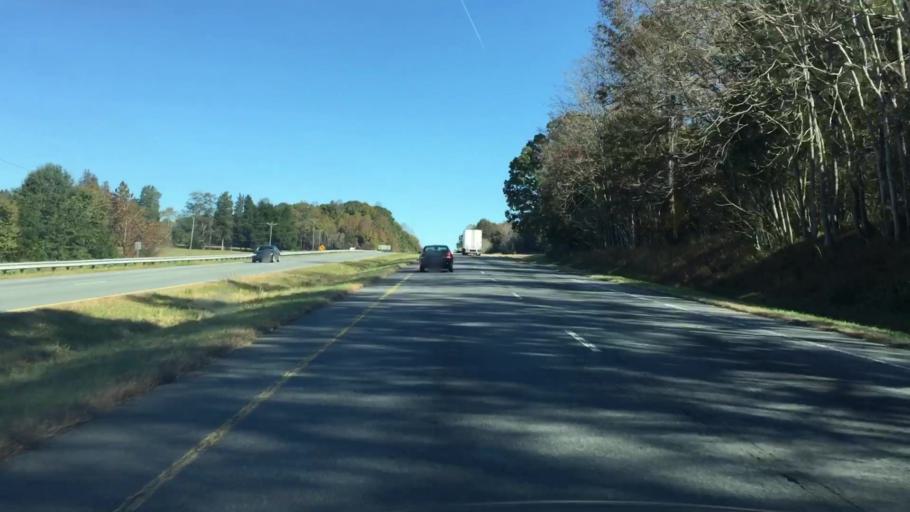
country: US
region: North Carolina
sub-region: Guilford County
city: McLeansville
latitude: 36.1840
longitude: -79.7069
